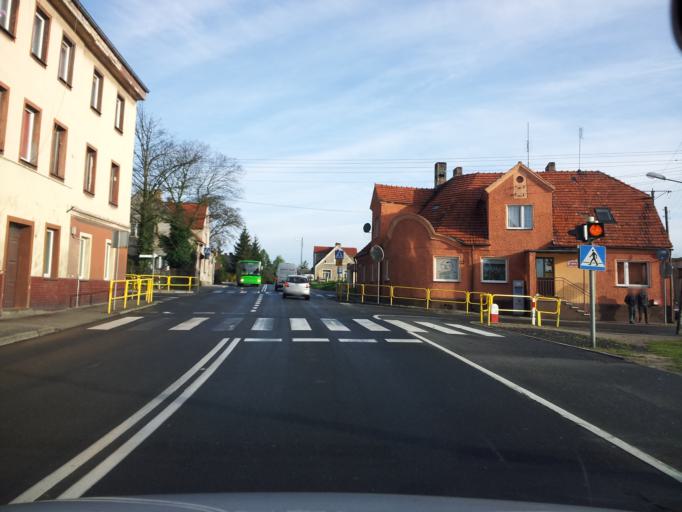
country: PL
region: Lubusz
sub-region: Powiat zarski
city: Zary
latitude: 51.7185
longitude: 15.1778
